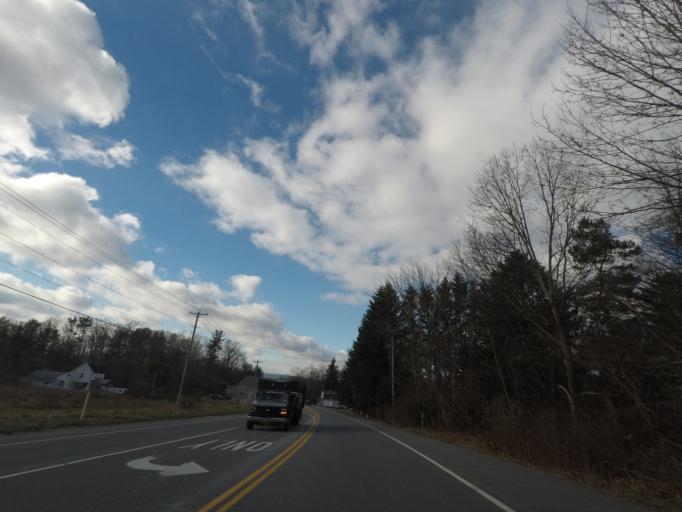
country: US
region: New York
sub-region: Schenectady County
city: East Glenville
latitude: 42.8670
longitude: -73.8918
